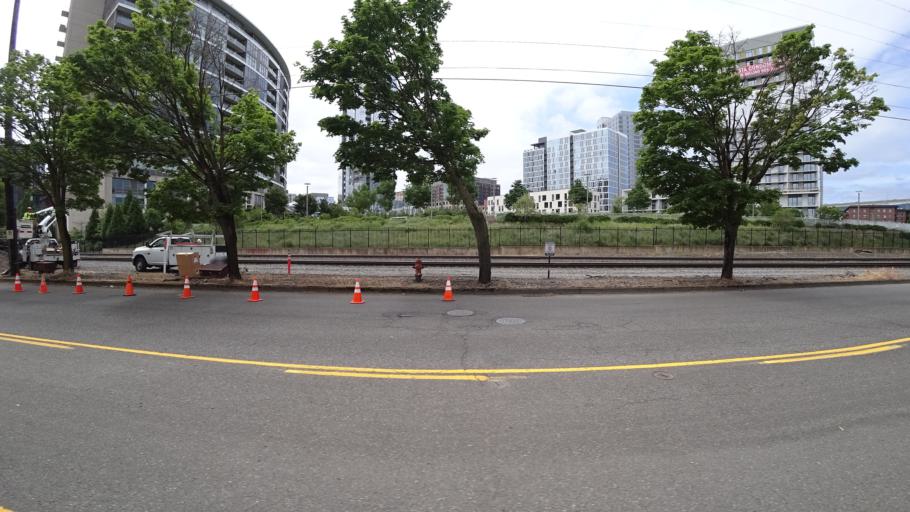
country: US
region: Oregon
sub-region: Multnomah County
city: Portland
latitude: 45.5335
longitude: -122.6809
